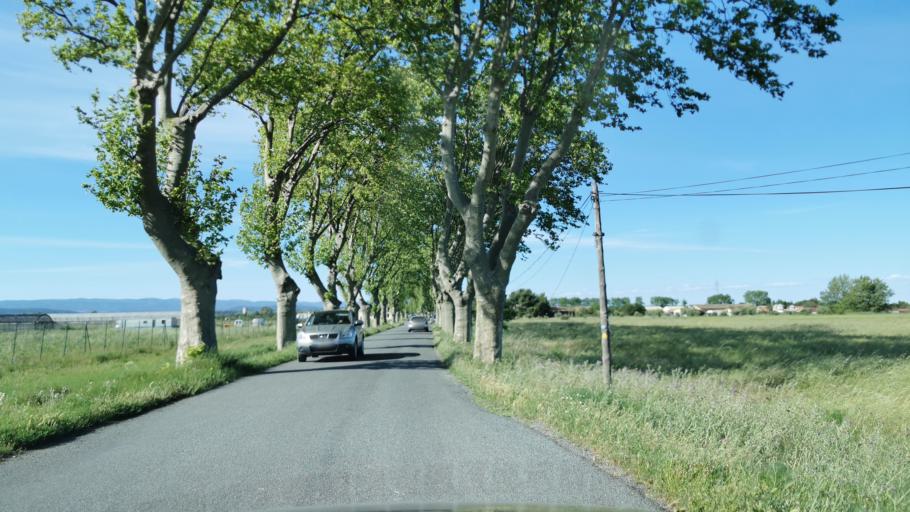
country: FR
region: Languedoc-Roussillon
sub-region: Departement de l'Aude
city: Canet
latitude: 43.2128
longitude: 2.8438
